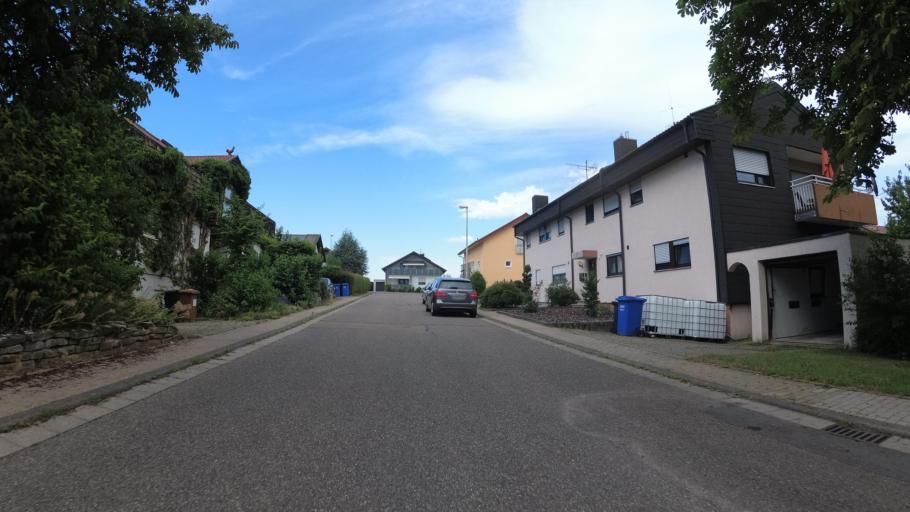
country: DE
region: Baden-Wuerttemberg
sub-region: Regierungsbezirk Stuttgart
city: Bad Rappenau
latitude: 49.2457
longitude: 9.1081
